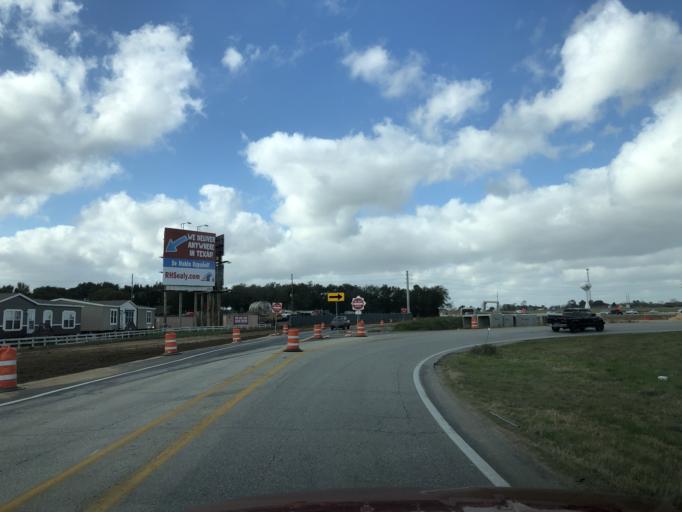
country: US
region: Texas
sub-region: Austin County
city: Sealy
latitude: 29.7623
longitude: -96.1566
